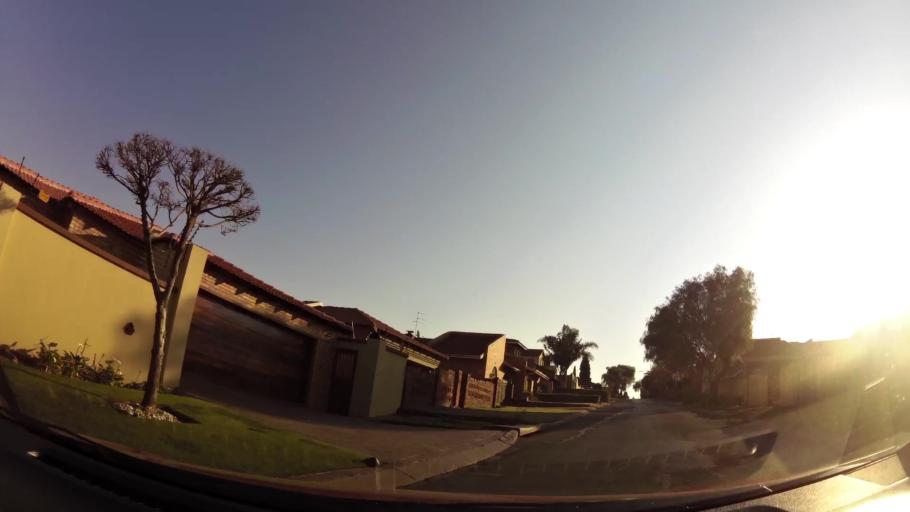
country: ZA
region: Gauteng
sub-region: City of Johannesburg Metropolitan Municipality
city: Johannesburg
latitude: -26.2569
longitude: 27.9591
